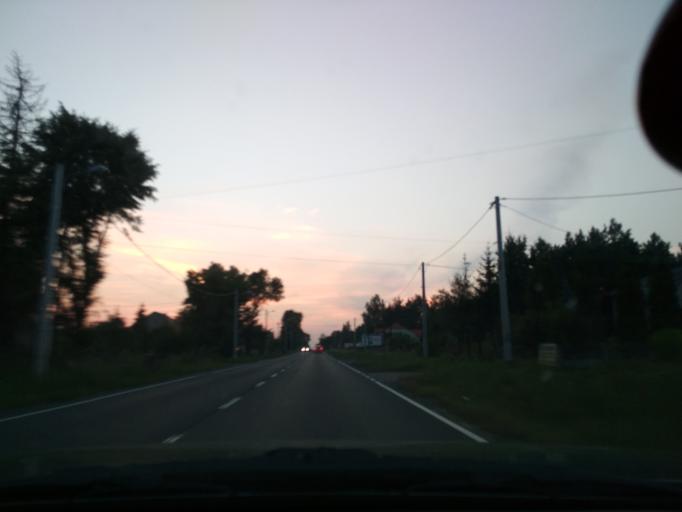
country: PL
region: Silesian Voivodeship
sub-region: Powiat zawiercianski
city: Ogrodzieniec
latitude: 50.4720
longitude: 19.4809
